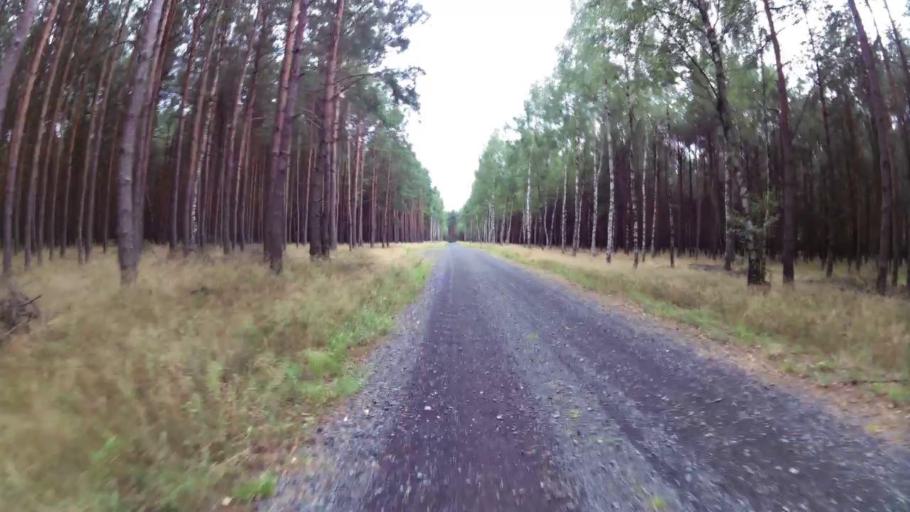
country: PL
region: West Pomeranian Voivodeship
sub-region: Powiat mysliborski
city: Debno
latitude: 52.7843
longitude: 14.7208
